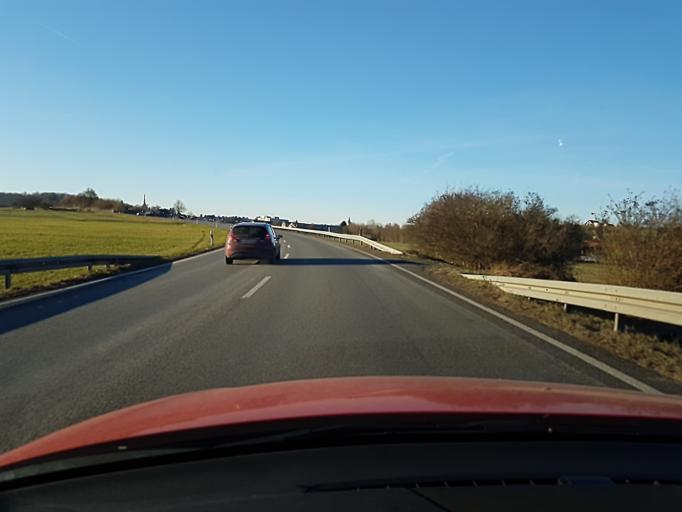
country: DE
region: Baden-Wuerttemberg
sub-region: Karlsruhe Region
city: Muhlacker
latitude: 48.9698
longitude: 8.8733
